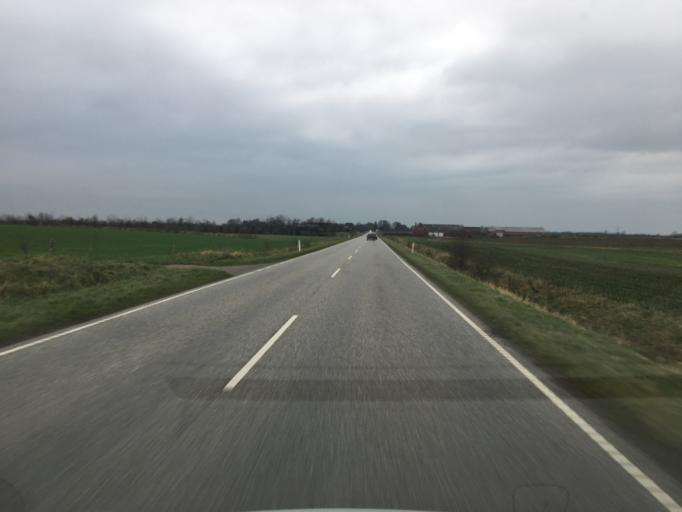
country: DK
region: South Denmark
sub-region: Aabenraa Kommune
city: Rodekro
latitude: 55.0100
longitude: 9.2709
